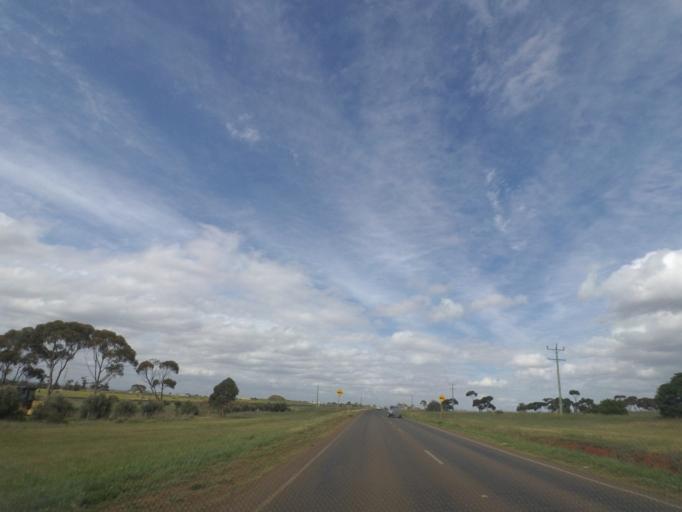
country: AU
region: Victoria
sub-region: Melton
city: Rockbank
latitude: -37.7472
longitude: 144.6897
